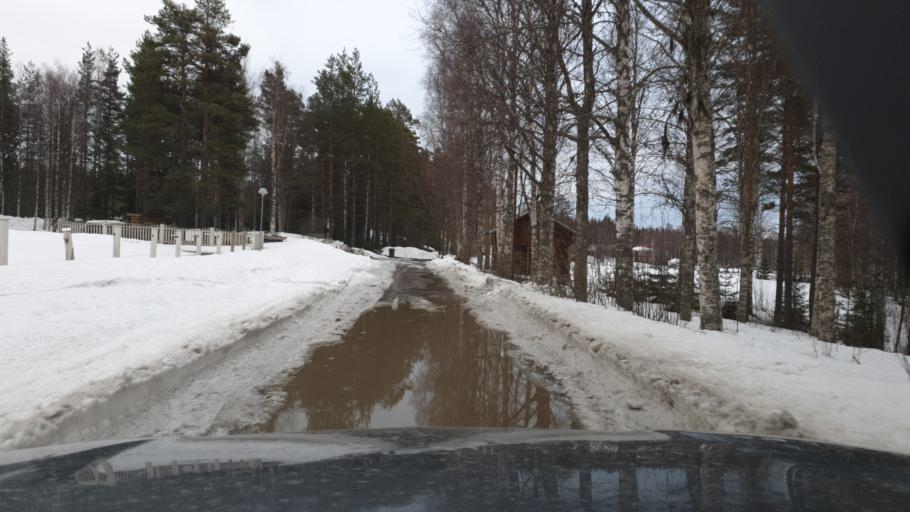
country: SE
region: Vaesternorrland
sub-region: Ange Kommun
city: Ange
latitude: 62.1873
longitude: 15.6601
